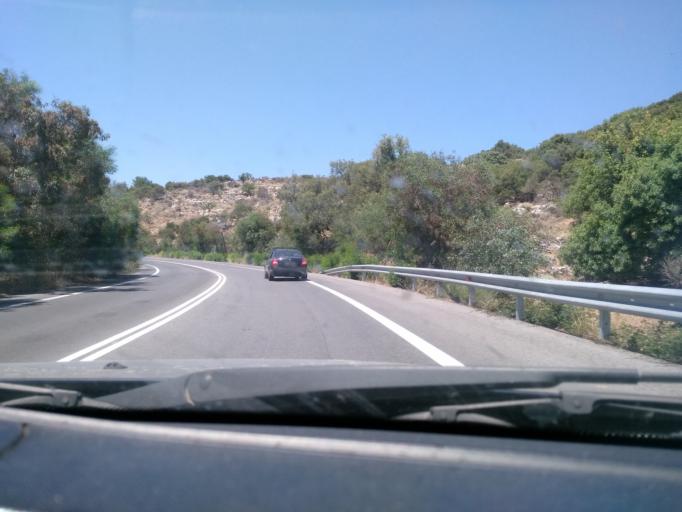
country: GR
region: Crete
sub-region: Nomos Chanias
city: Kalivai
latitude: 35.4268
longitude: 24.1706
